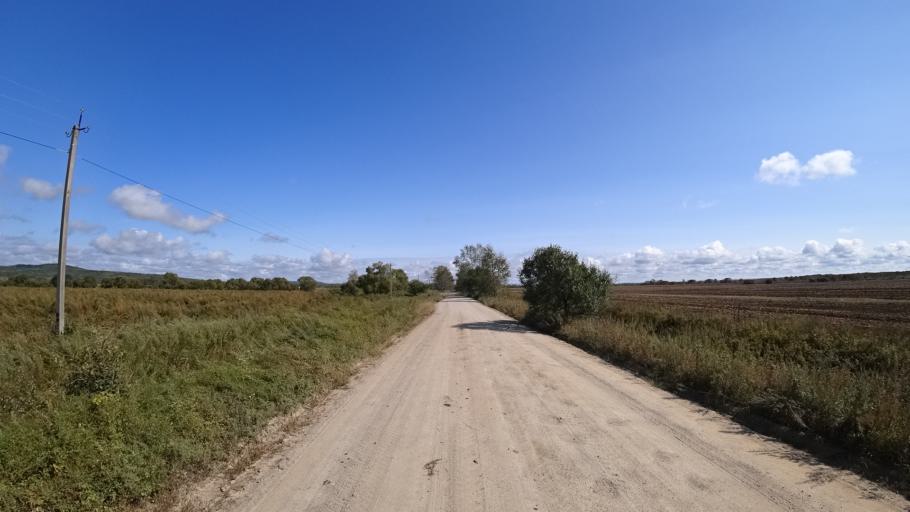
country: RU
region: Amur
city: Arkhara
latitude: 49.4120
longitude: 130.1682
